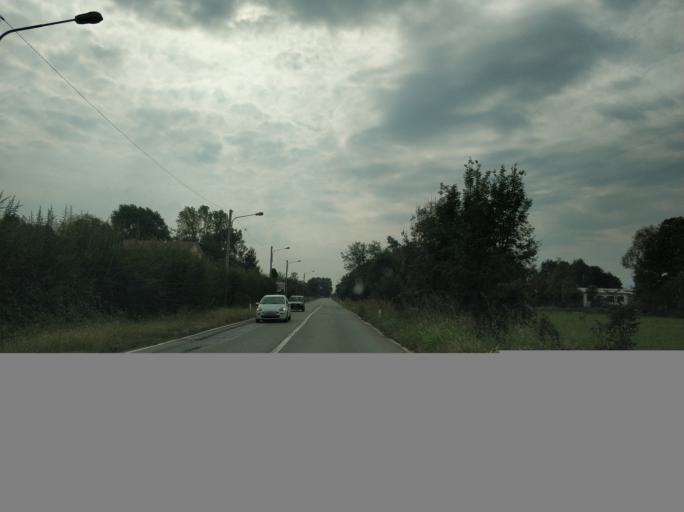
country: IT
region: Piedmont
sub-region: Provincia di Torino
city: Grosso
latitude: 45.2589
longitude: 7.5624
